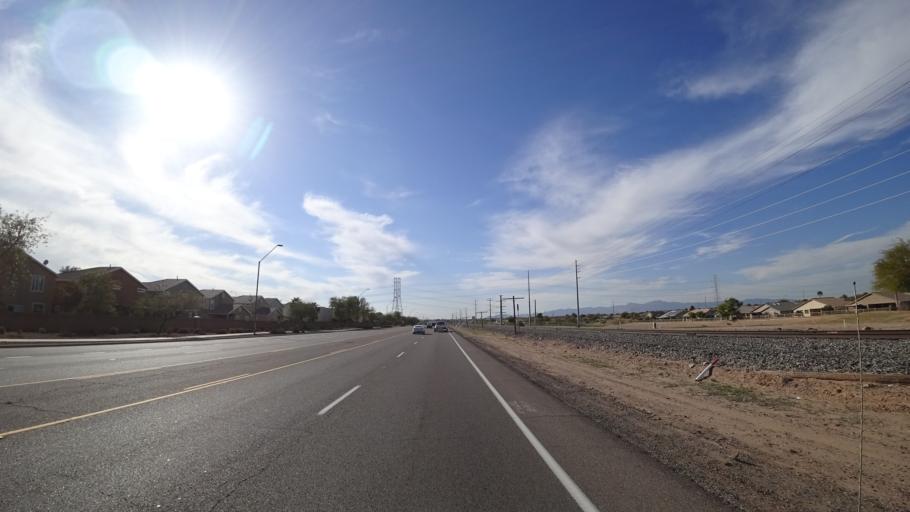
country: US
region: Arizona
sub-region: Maricopa County
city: Avondale
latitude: 33.4355
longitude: -112.3160
